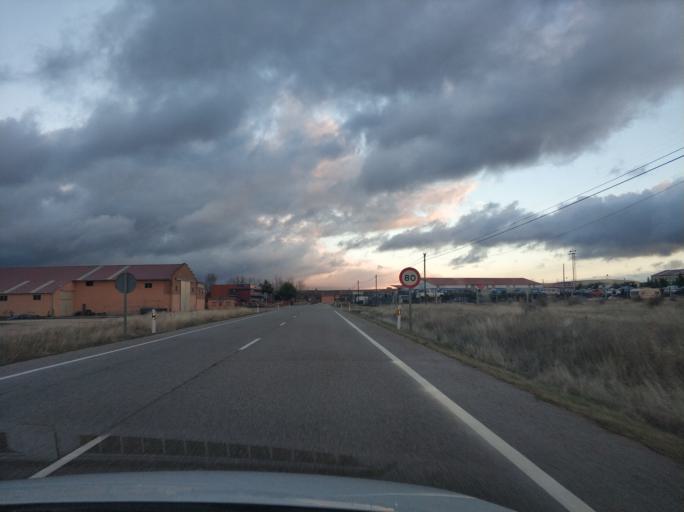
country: ES
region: Castille and Leon
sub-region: Provincia de Segovia
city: Ayllon
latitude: 41.4155
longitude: -3.3926
